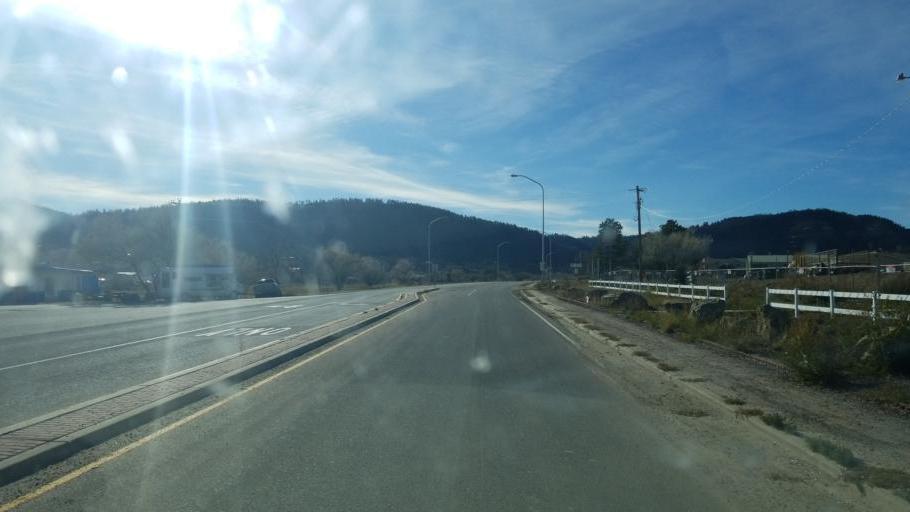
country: US
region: New Mexico
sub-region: Rio Arriba County
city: Dulce
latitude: 36.9339
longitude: -106.9880
